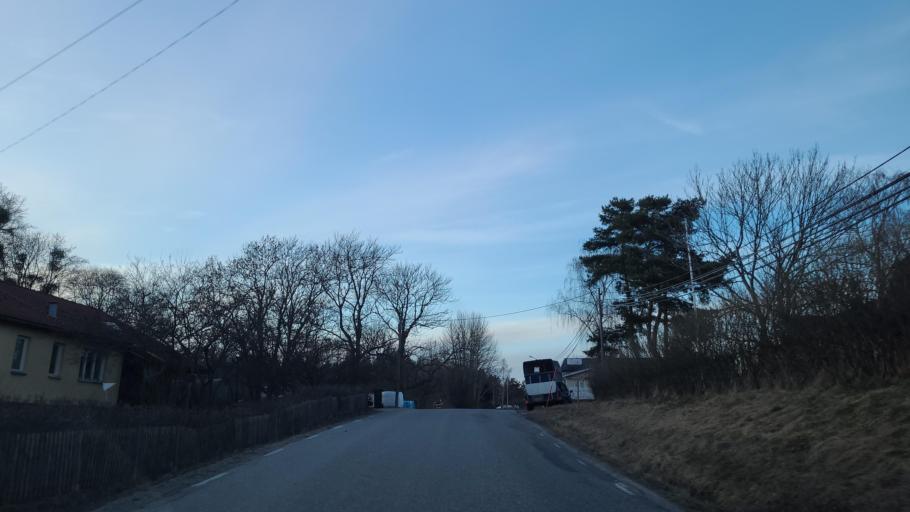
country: SE
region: Stockholm
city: Stenhamra
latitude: 59.4023
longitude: 17.6569
